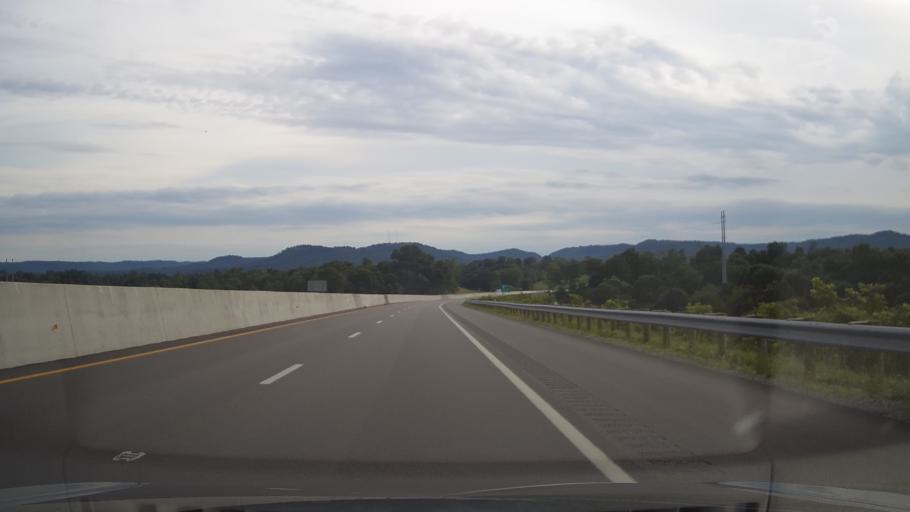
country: US
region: Ohio
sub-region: Scioto County
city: Lucasville
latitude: 38.8937
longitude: -82.9822
